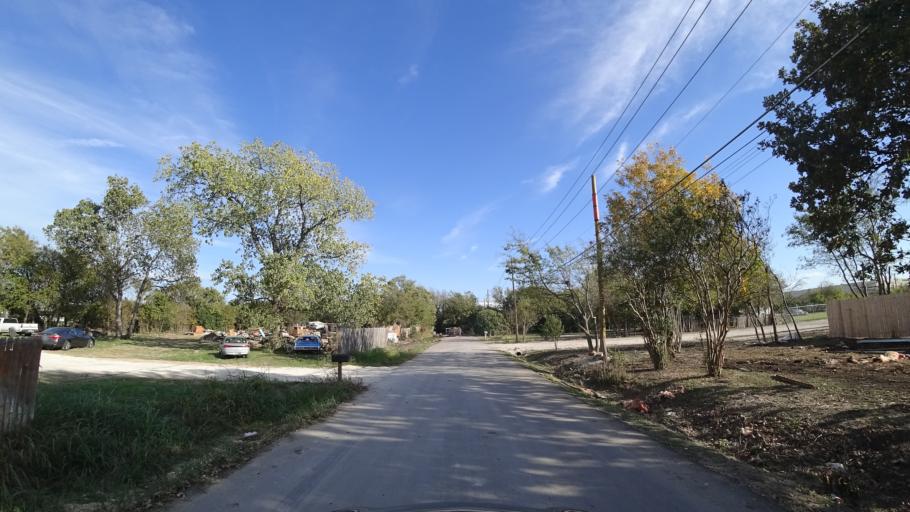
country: US
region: Texas
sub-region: Travis County
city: Wells Branch
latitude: 30.4722
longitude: -97.6793
